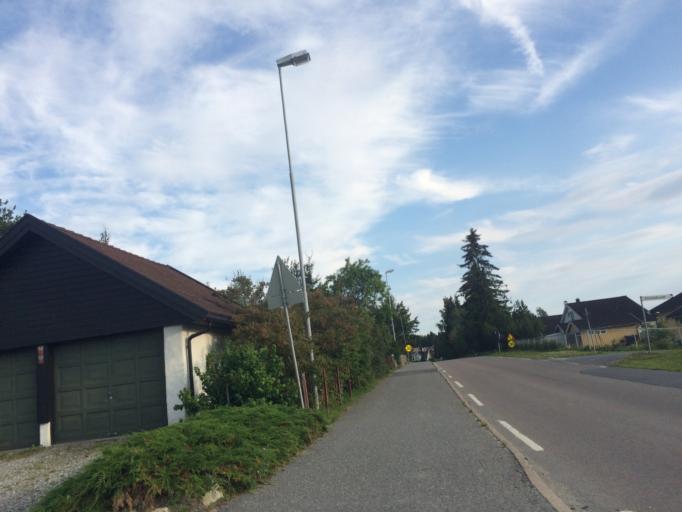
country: NO
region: Akershus
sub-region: Ski
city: Ski
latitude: 59.7079
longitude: 10.8436
